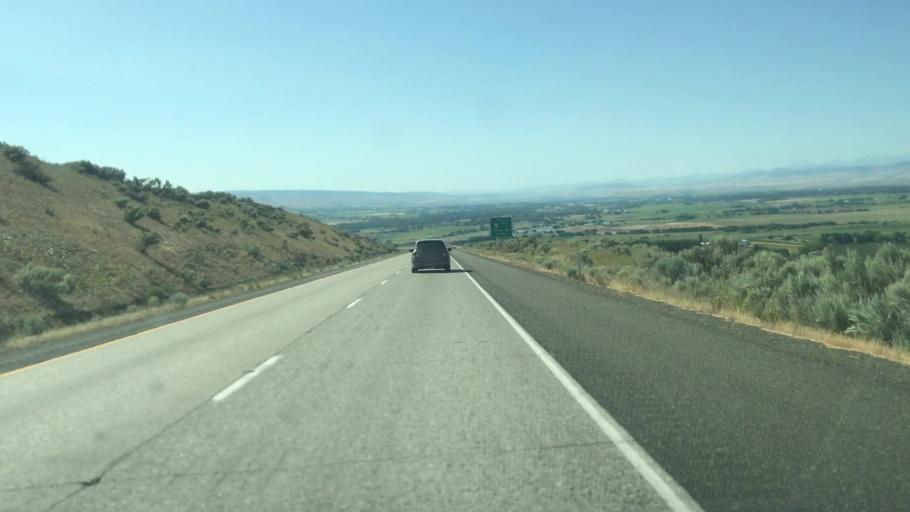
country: US
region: Washington
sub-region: Kittitas County
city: Kittitas
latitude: 46.9094
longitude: -120.4638
